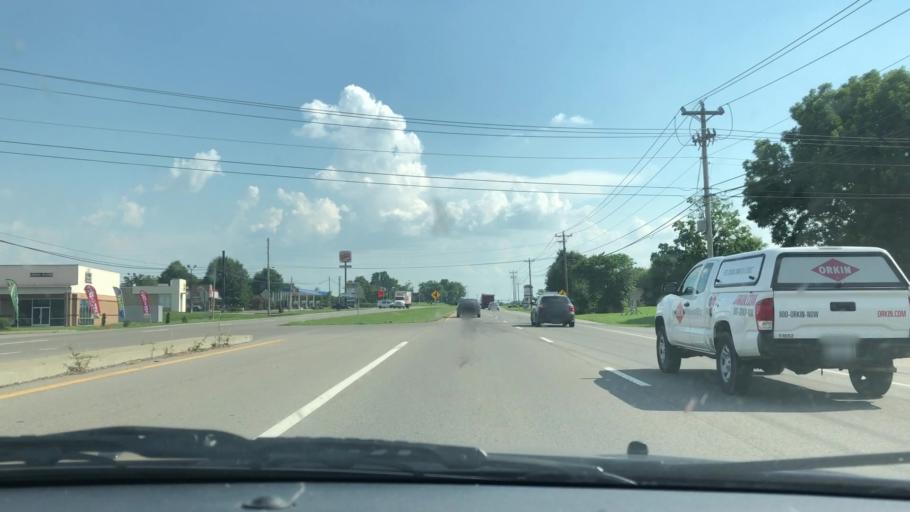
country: US
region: Tennessee
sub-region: Maury County
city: Spring Hill
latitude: 35.7113
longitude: -86.9740
